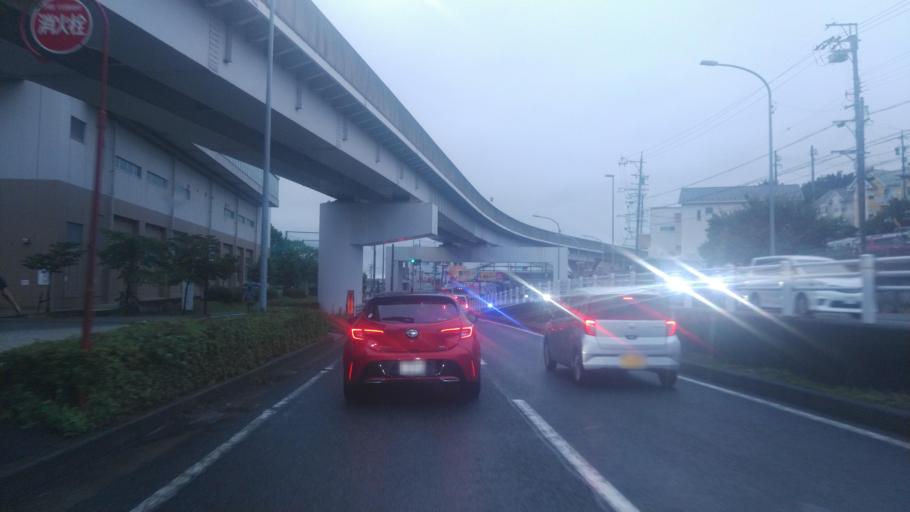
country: JP
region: Aichi
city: Kasugai
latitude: 35.2187
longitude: 136.9826
